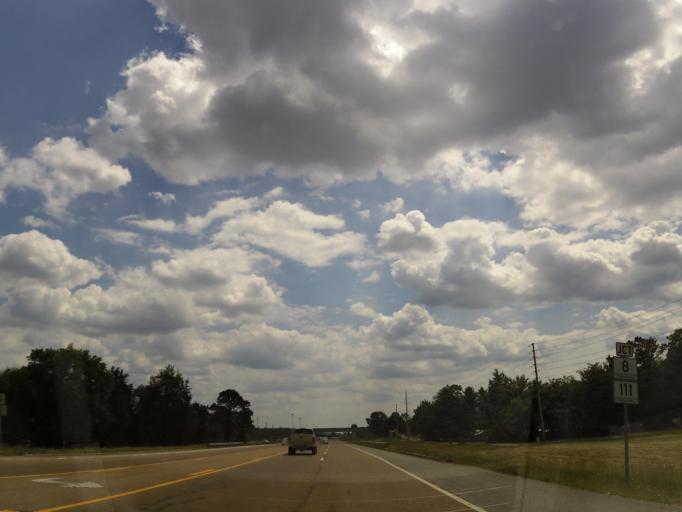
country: US
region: Tennessee
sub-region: Sequatchie County
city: Dunlap
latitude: 35.3992
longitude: -85.3722
